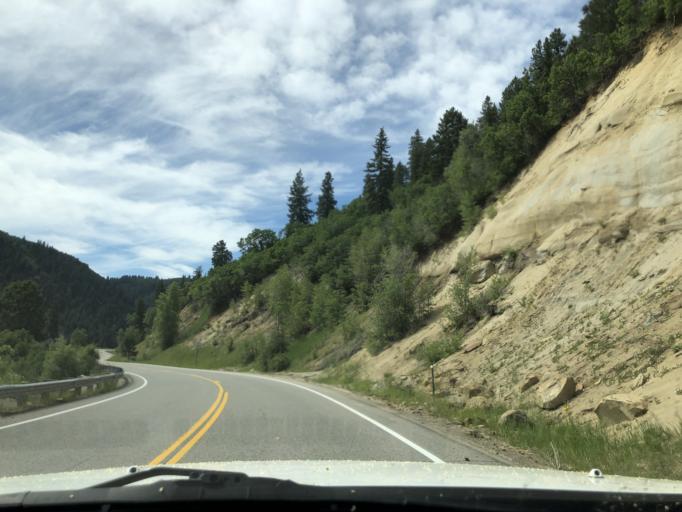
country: US
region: Colorado
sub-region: Delta County
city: Paonia
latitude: 38.9684
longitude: -107.3403
